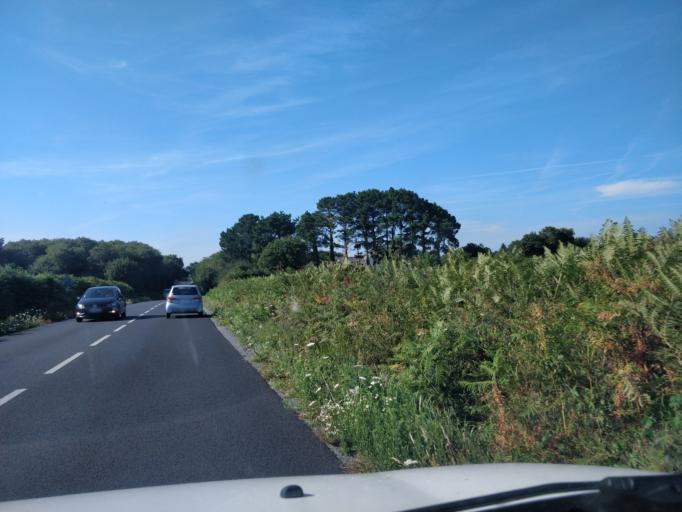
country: FR
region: Brittany
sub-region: Departement des Cotes-d'Armor
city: Tregastel
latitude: 48.7968
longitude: -3.4964
